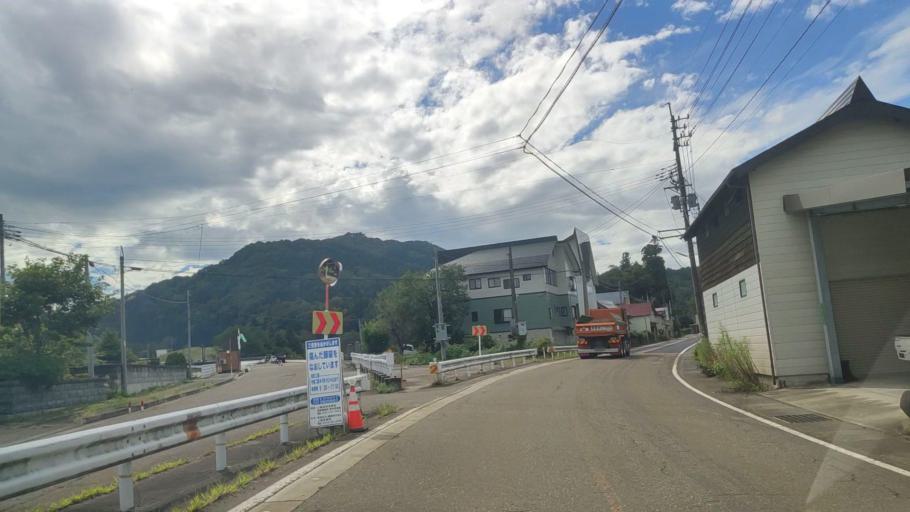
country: JP
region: Niigata
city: Arai
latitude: 36.9596
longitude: 138.2709
